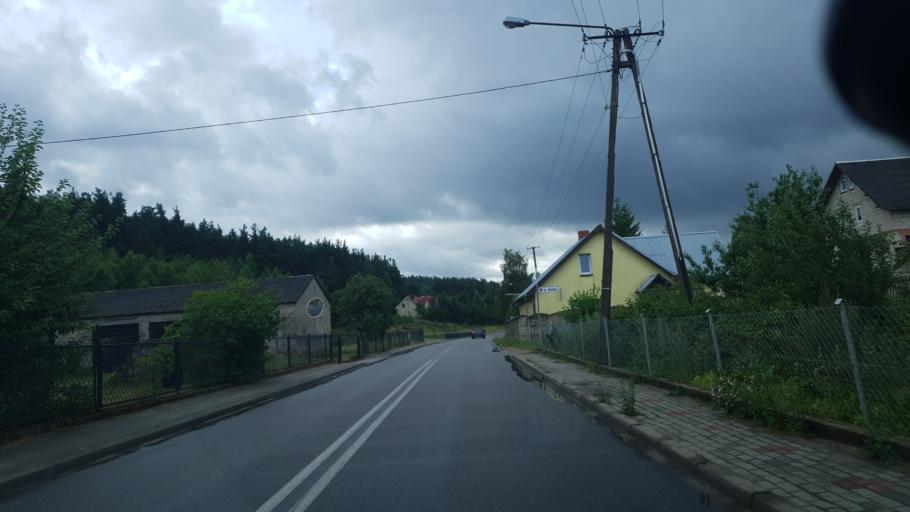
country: PL
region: Pomeranian Voivodeship
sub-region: Powiat kartuski
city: Stezyca
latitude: 54.2359
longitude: 17.9841
